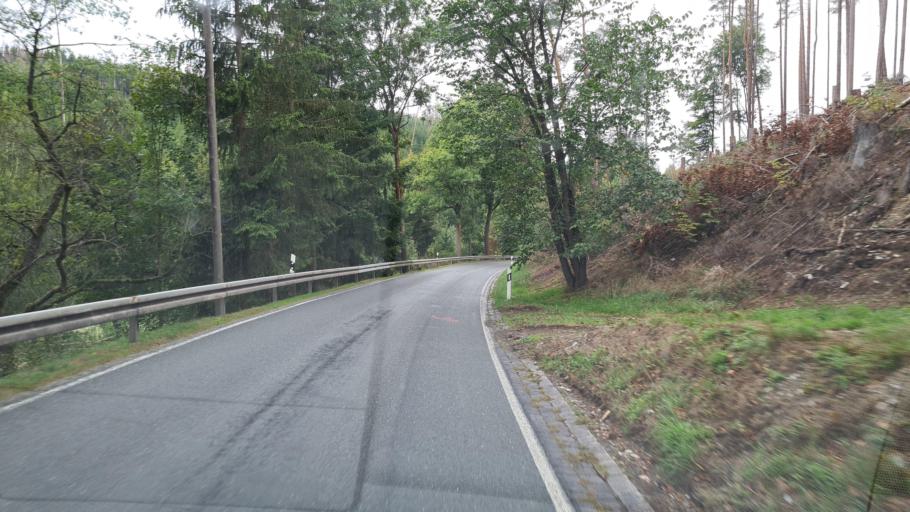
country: DE
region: Thuringia
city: Leutenberg
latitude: 50.5287
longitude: 11.5029
